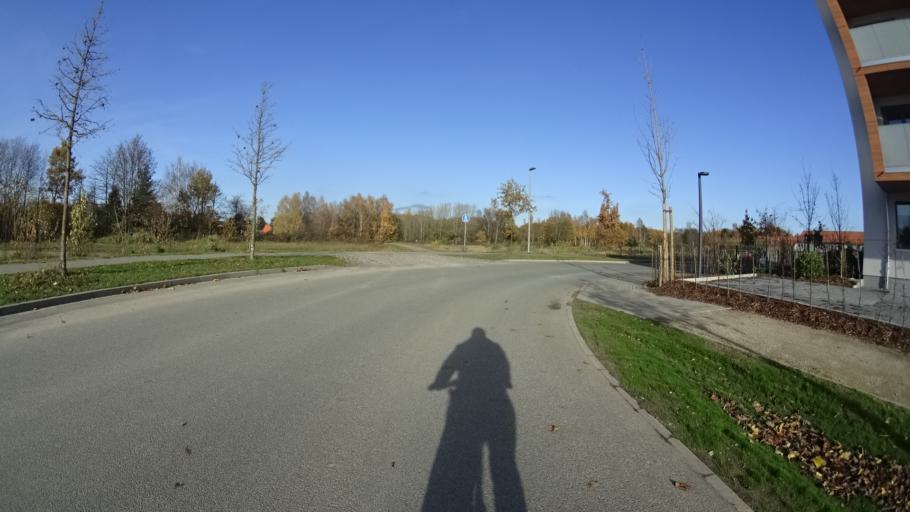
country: DE
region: Lower Saxony
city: Lueneburg
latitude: 53.2565
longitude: 10.4243
